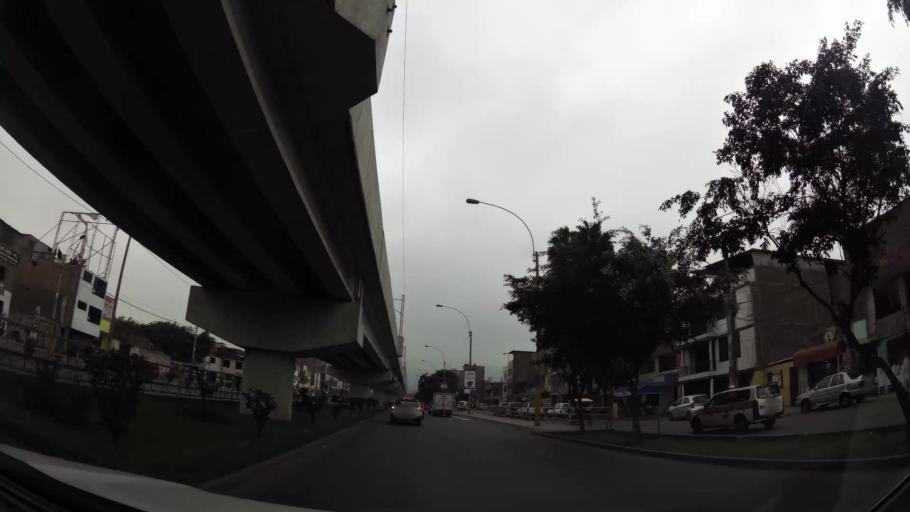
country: PE
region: Lima
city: Lima
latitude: -12.0237
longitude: -77.0081
